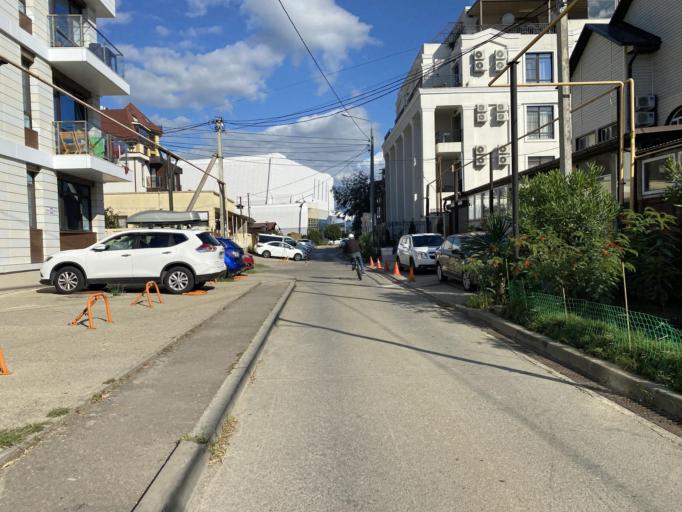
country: RU
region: Krasnodarskiy
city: Adler
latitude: 43.4103
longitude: 39.9594
